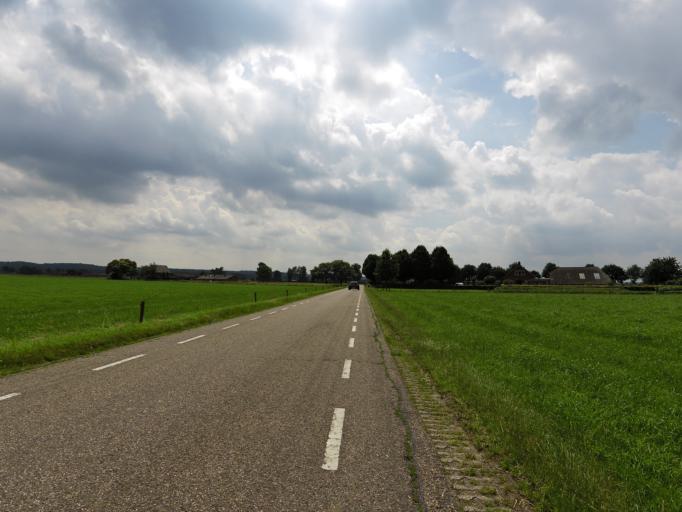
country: NL
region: Gelderland
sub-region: Gemeente Montferland
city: s-Heerenberg
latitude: 51.9392
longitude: 6.2025
